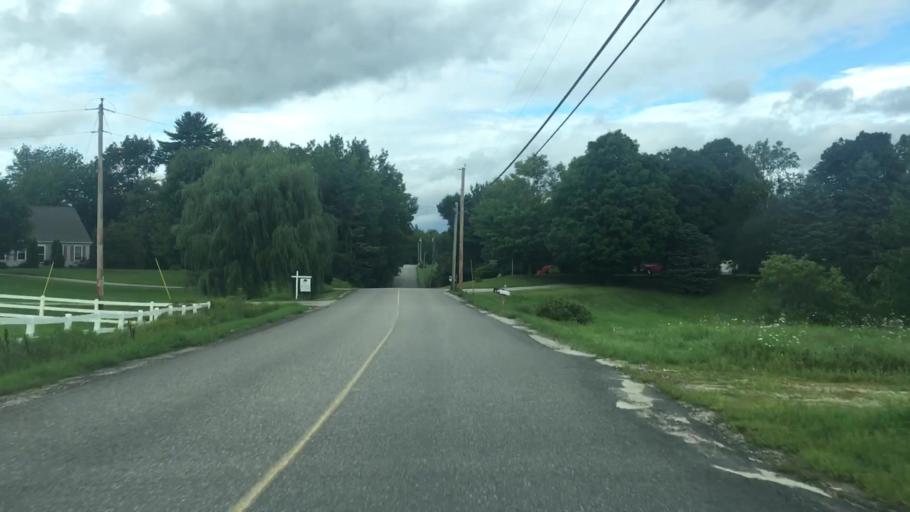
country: US
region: Maine
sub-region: York County
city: Dayton
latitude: 43.5379
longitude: -70.5779
